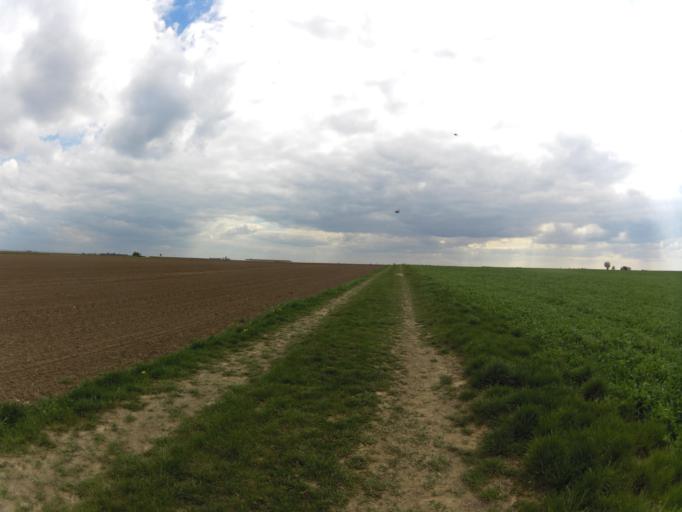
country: DE
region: Bavaria
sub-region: Regierungsbezirk Unterfranken
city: Giebelstadt
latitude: 49.6481
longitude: 9.9444
